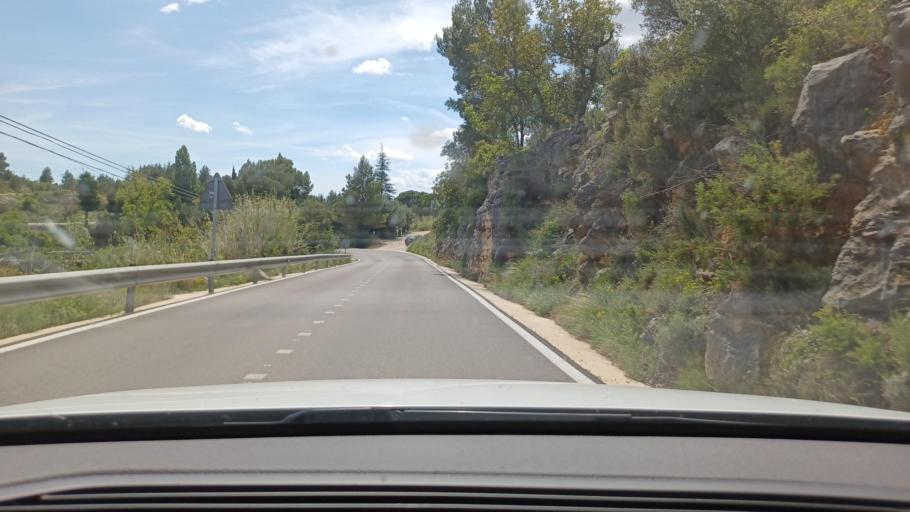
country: ES
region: Valencia
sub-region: Provincia de Castello
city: Rosell
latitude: 40.6488
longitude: 0.2688
